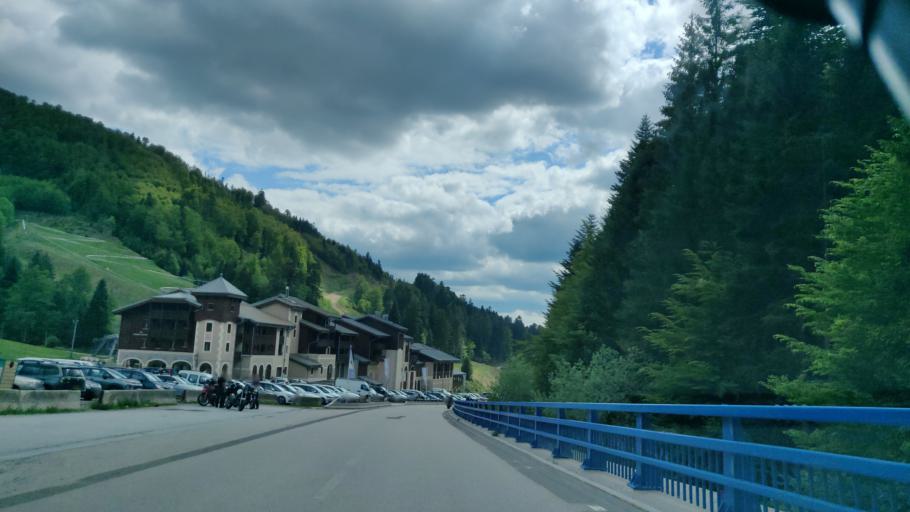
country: FR
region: Lorraine
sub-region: Departement des Vosges
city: Xonrupt-Longemer
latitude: 48.0389
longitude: 6.9720
